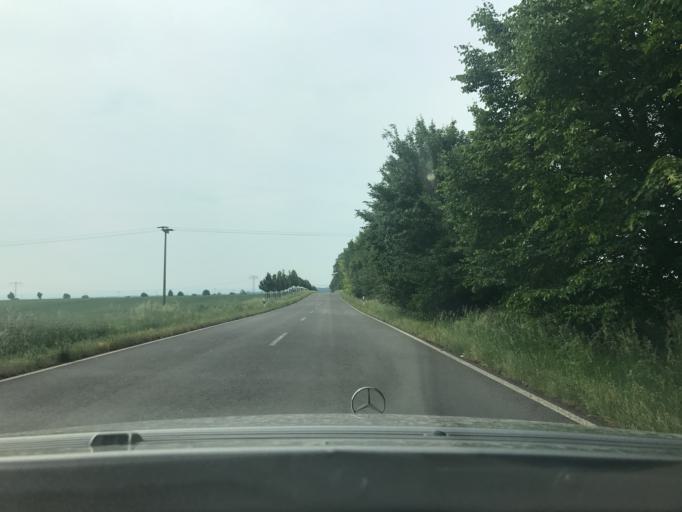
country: DE
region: Thuringia
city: Muehlhausen
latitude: 51.2269
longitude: 10.4921
